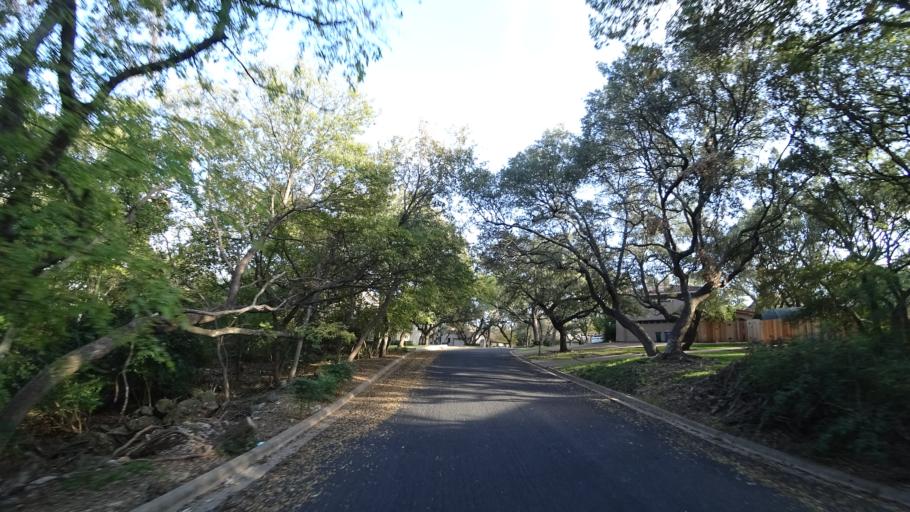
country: US
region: Texas
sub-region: Williamson County
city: Anderson Mill
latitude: 30.4390
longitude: -97.8023
